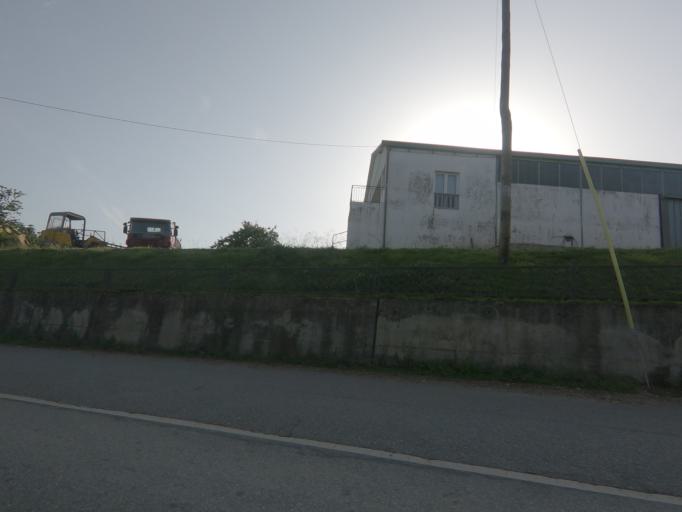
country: PT
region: Vila Real
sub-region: Sabrosa
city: Sabrosa
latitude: 41.2593
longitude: -7.4688
